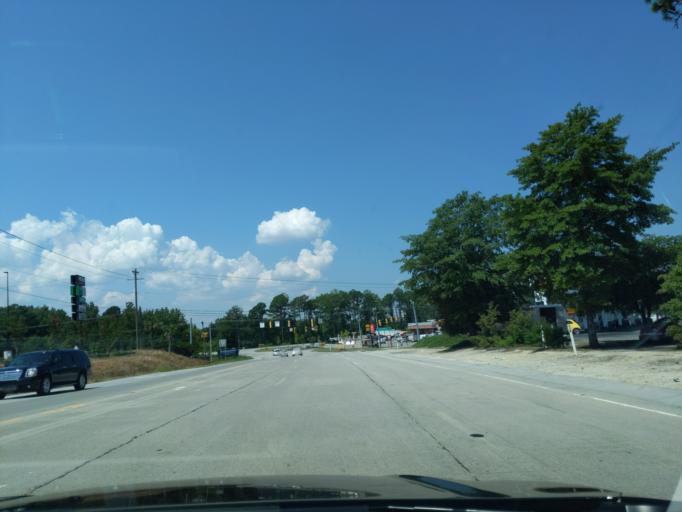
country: US
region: South Carolina
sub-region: Richland County
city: Columbia
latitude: 33.9540
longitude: -80.9907
